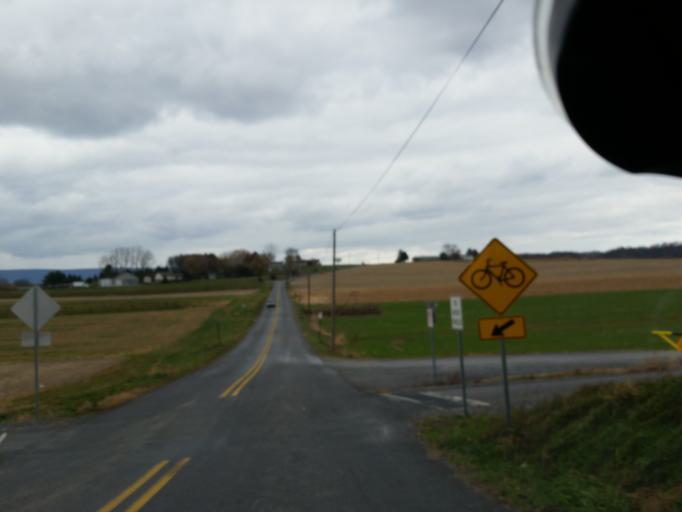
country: US
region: Pennsylvania
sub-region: Union County
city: Linntown
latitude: 40.9495
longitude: -76.9549
